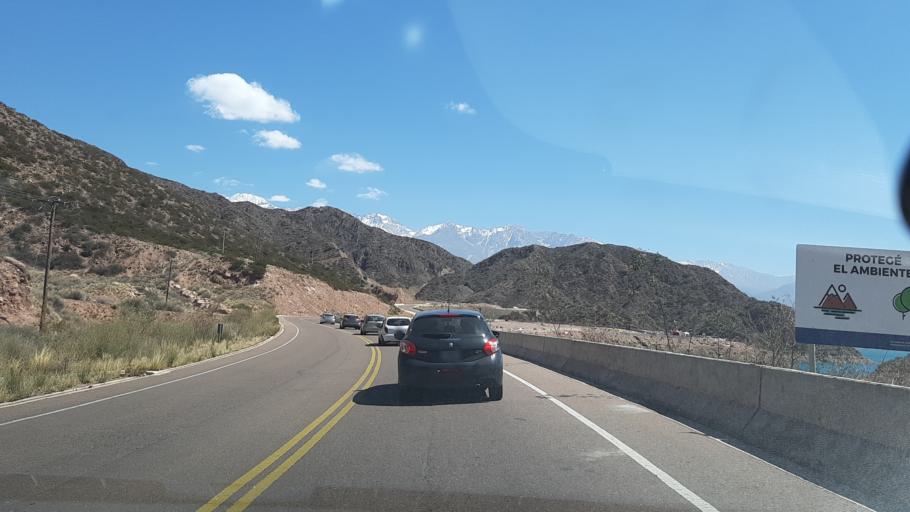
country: AR
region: Mendoza
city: Lujan de Cuyo
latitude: -32.9958
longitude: -69.1419
